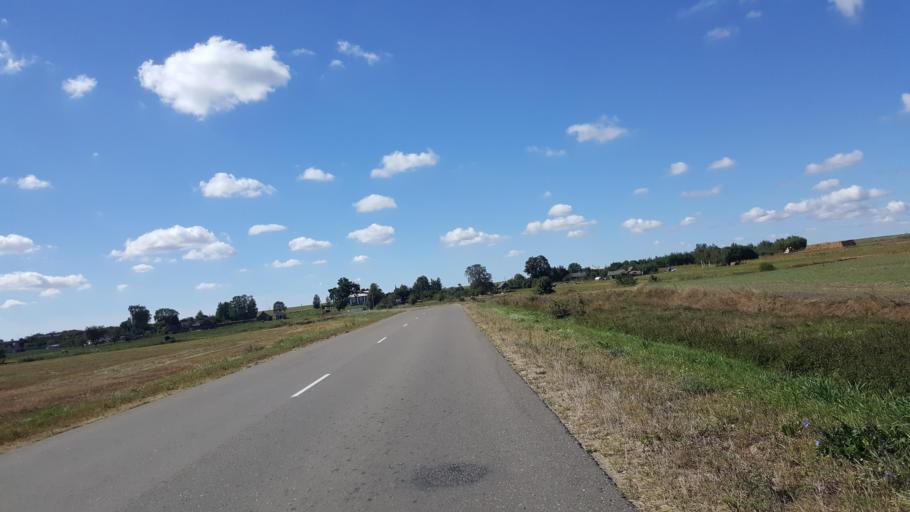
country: BY
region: Brest
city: Vysokaye
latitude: 52.3599
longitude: 23.5131
